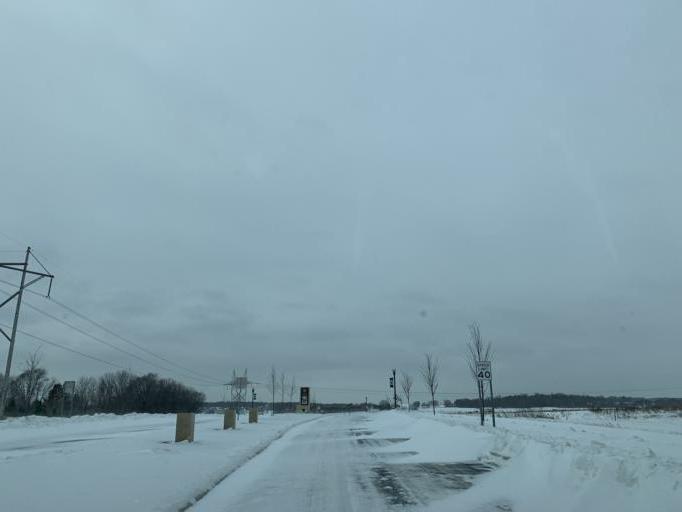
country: US
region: Minnesota
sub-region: Washington County
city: Cottage Grove
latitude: 44.8559
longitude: -92.9041
